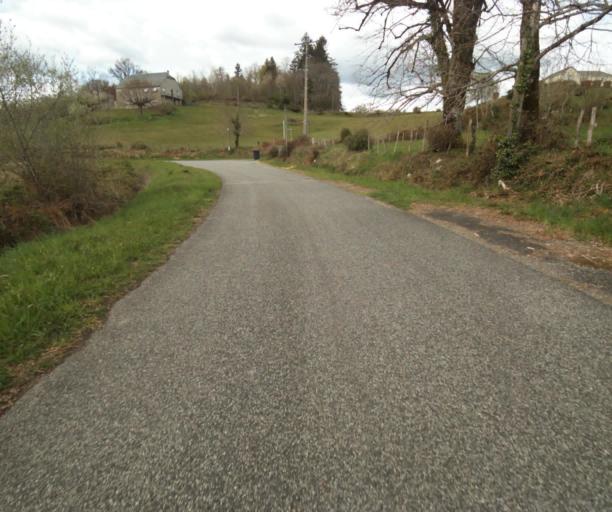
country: FR
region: Limousin
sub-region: Departement de la Correze
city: Argentat
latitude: 45.1893
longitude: 1.9523
